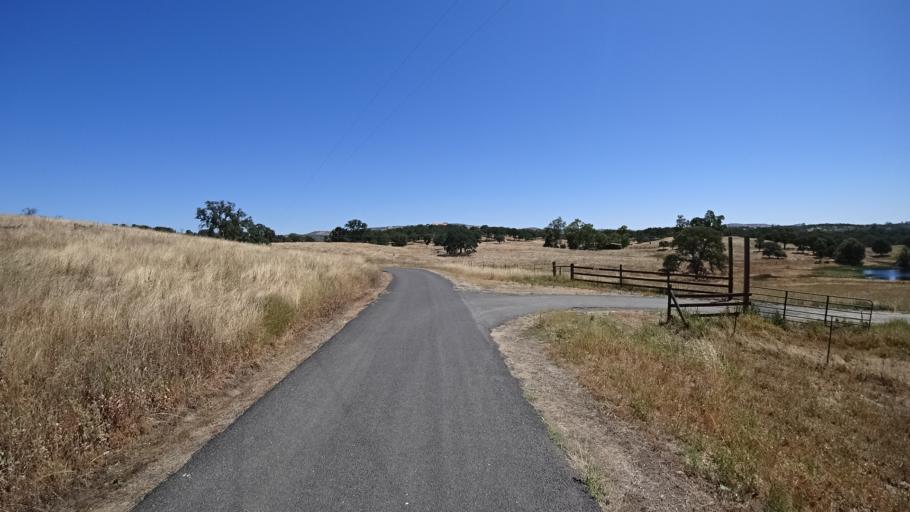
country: US
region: California
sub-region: Calaveras County
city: Copperopolis
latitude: 37.9508
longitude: -120.6737
